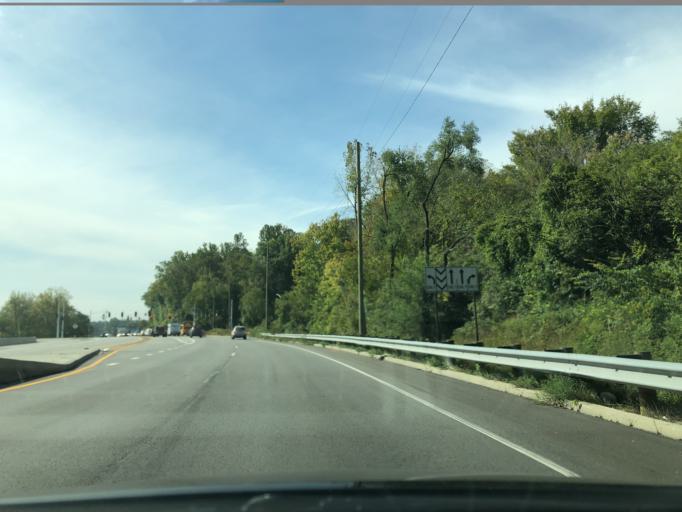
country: US
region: Ohio
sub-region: Hamilton County
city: Fairfax
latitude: 39.1651
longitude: -84.4012
